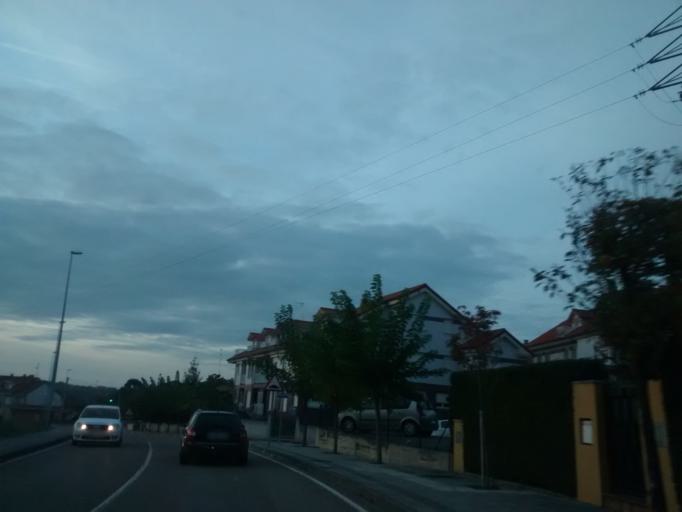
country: ES
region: Cantabria
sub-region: Provincia de Cantabria
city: Santa Cruz de Bezana
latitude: 43.4280
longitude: -3.9413
